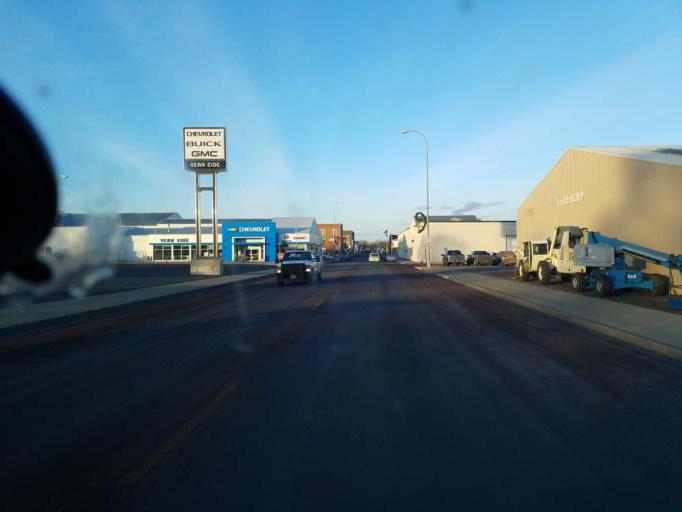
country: US
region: South Dakota
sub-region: Davison County
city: Mitchell
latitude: 43.7095
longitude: -98.0218
